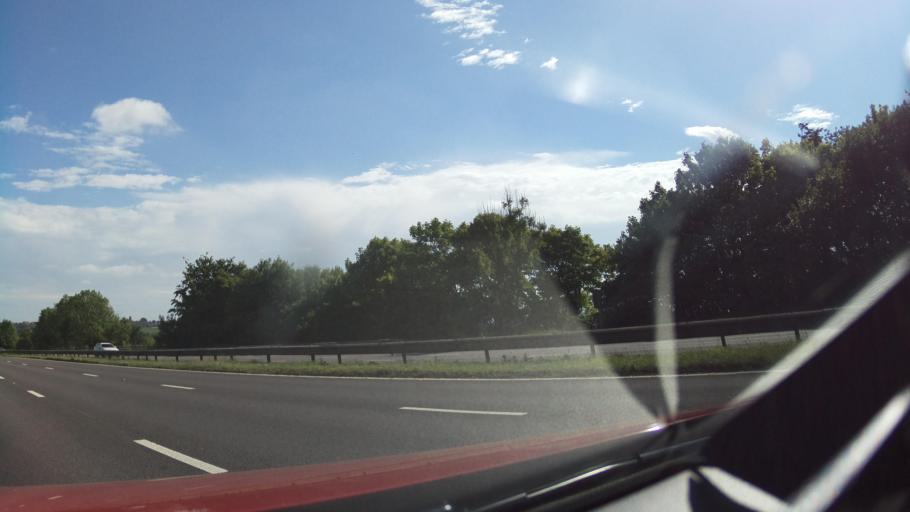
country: GB
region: England
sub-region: Borough of Wigan
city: Haigh
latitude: 53.6141
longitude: -2.5836
